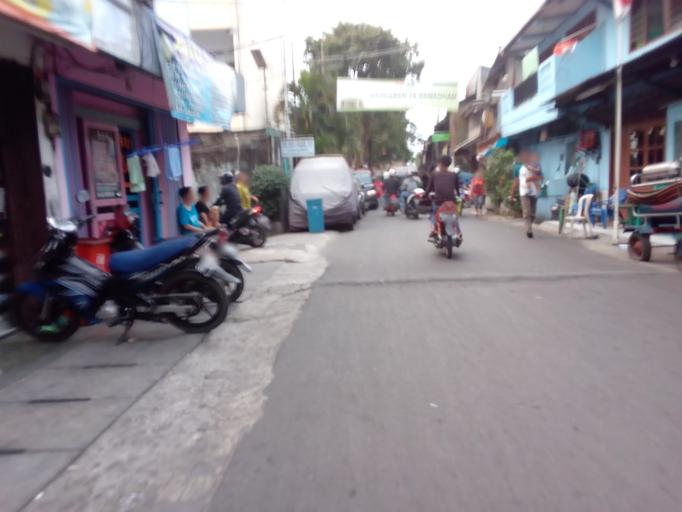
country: ID
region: Jakarta Raya
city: Jakarta
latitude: -6.1648
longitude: 106.8015
